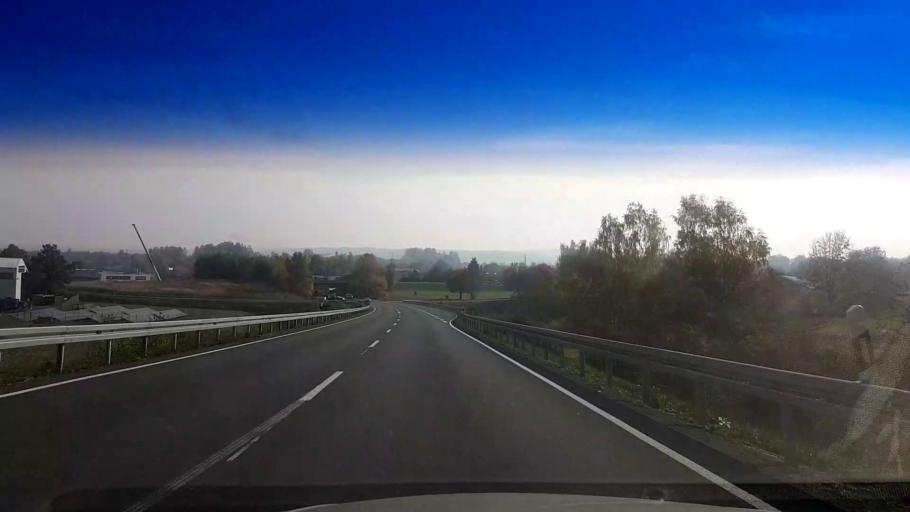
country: DE
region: Bavaria
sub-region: Upper Franconia
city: Marktredwitz
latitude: 50.0167
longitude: 12.0925
